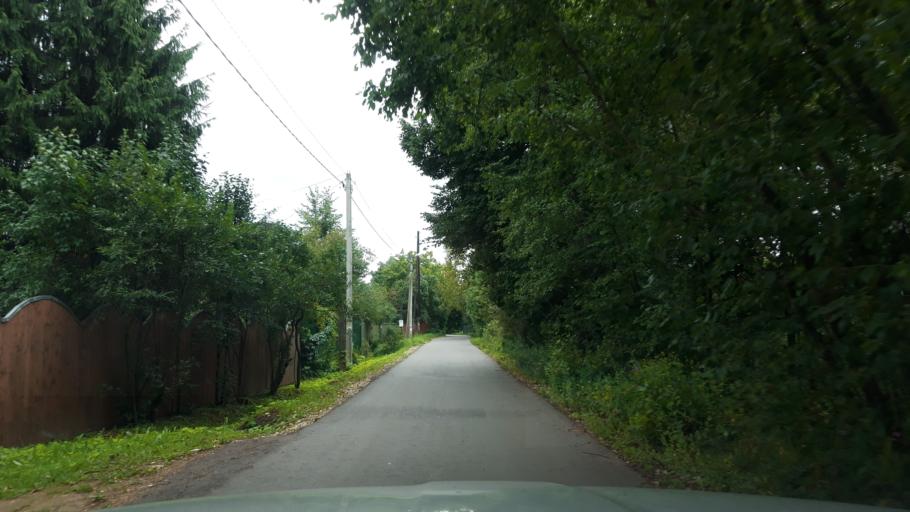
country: RU
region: Moskovskaya
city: Povarovo
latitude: 56.0751
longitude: 37.0661
